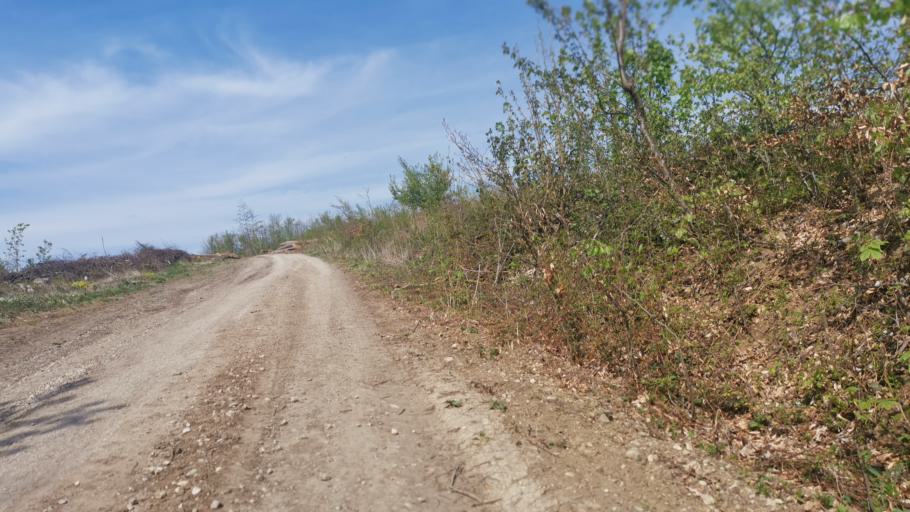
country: SK
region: Trnavsky
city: Smolenice
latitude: 48.5642
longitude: 17.3569
